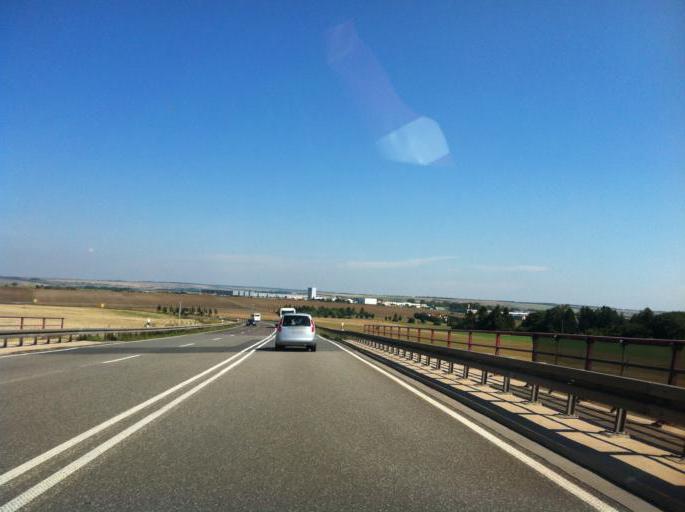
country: DE
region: Thuringia
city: Bad Langensalza
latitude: 51.1111
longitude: 10.6189
